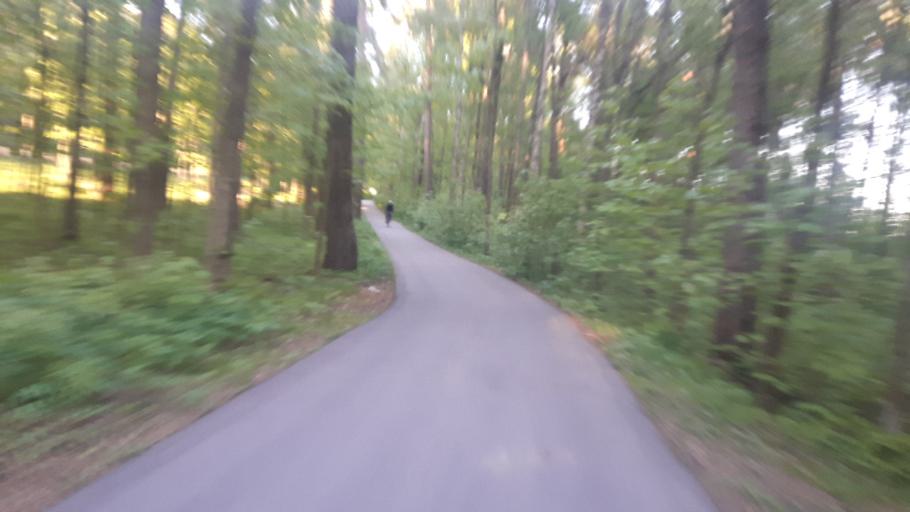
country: RU
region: Leningrad
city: Roshchino
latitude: 60.1925
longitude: 29.6354
